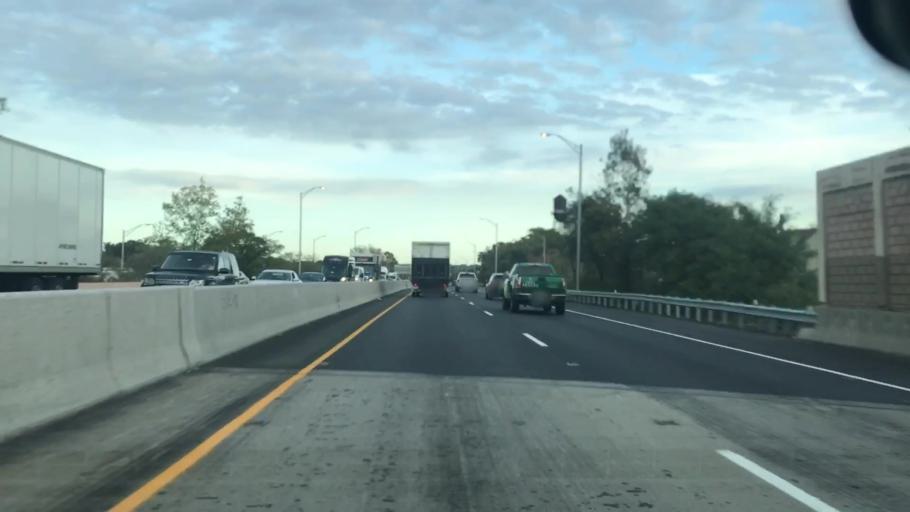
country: US
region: New Jersey
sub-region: Bergen County
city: Garfield
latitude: 40.8790
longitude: -74.1226
